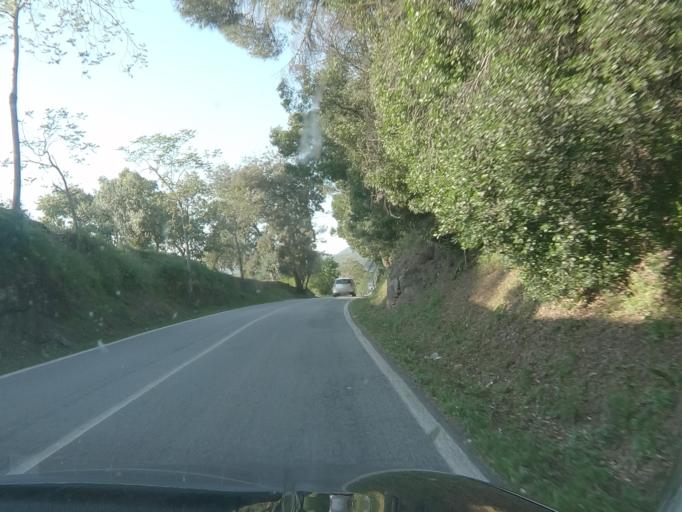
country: PT
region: Portalegre
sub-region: Portalegre
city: Portalegre
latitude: 39.3175
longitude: -7.4396
